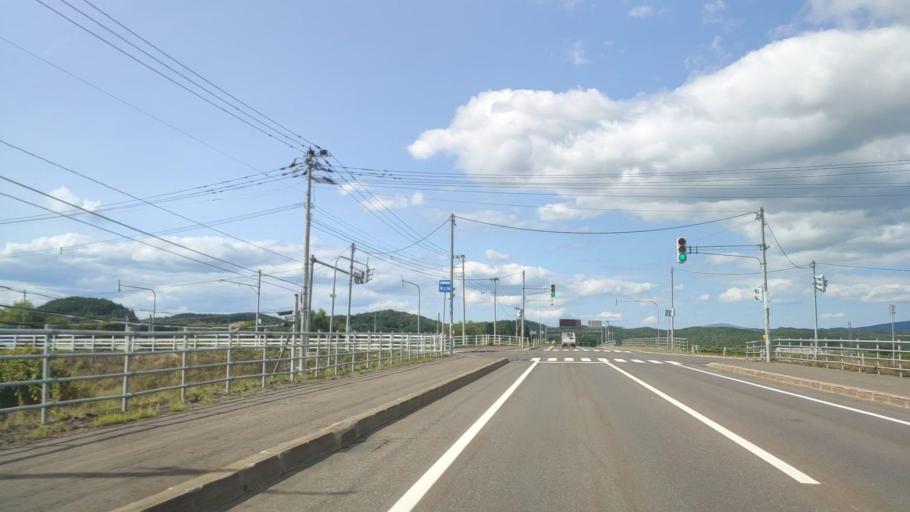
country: JP
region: Hokkaido
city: Nayoro
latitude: 44.3709
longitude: 142.4361
